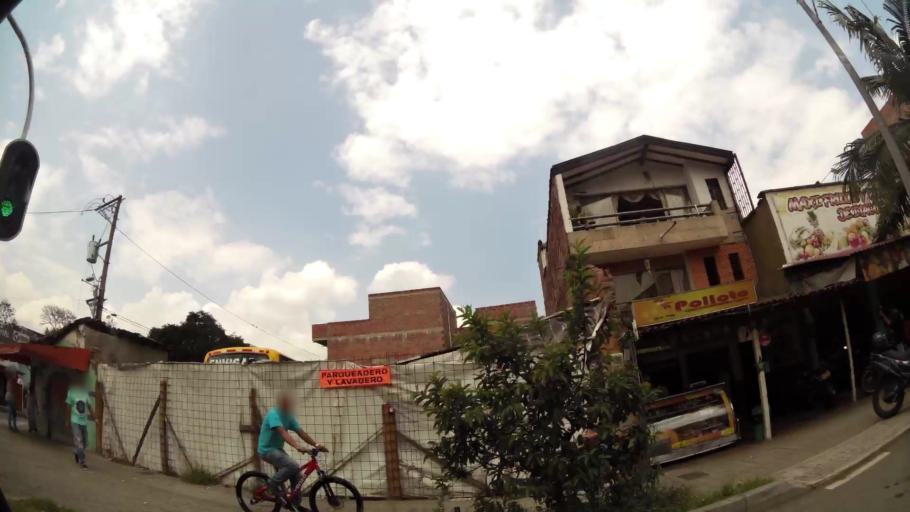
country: CO
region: Antioquia
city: Itagui
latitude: 6.1837
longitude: -75.5997
